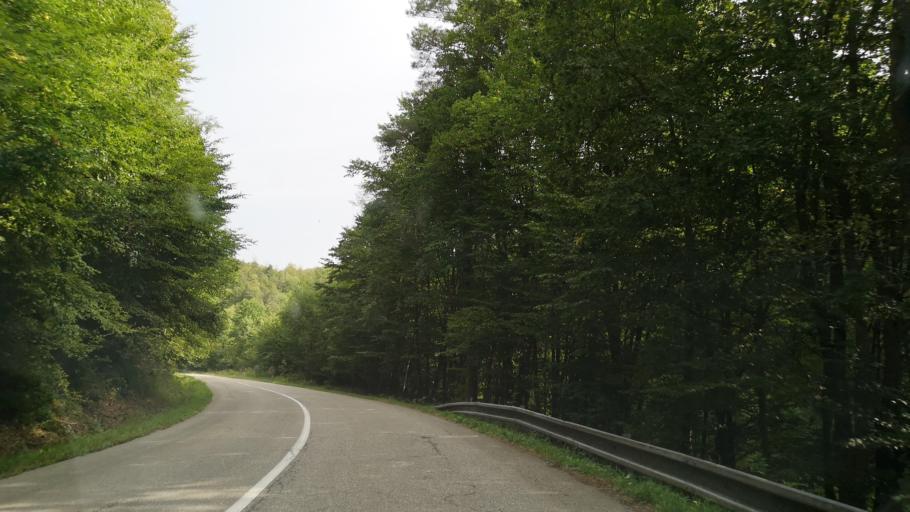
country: SK
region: Banskobystricky
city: Revuca
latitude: 48.5888
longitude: 20.0481
